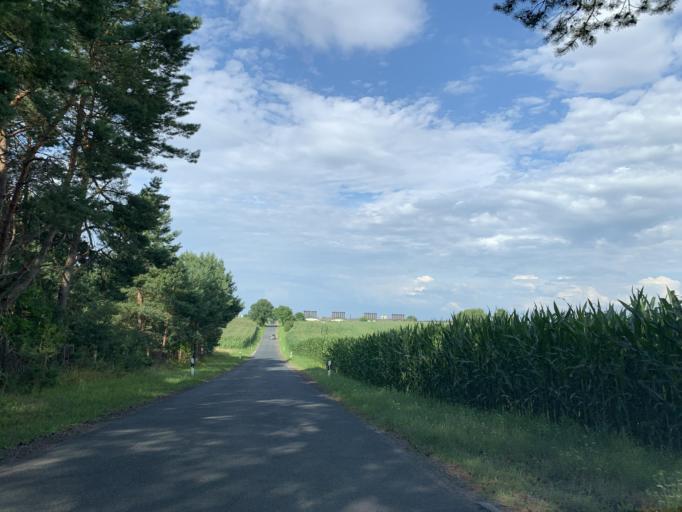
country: DE
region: Mecklenburg-Vorpommern
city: Carpin
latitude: 53.3864
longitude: 13.2153
